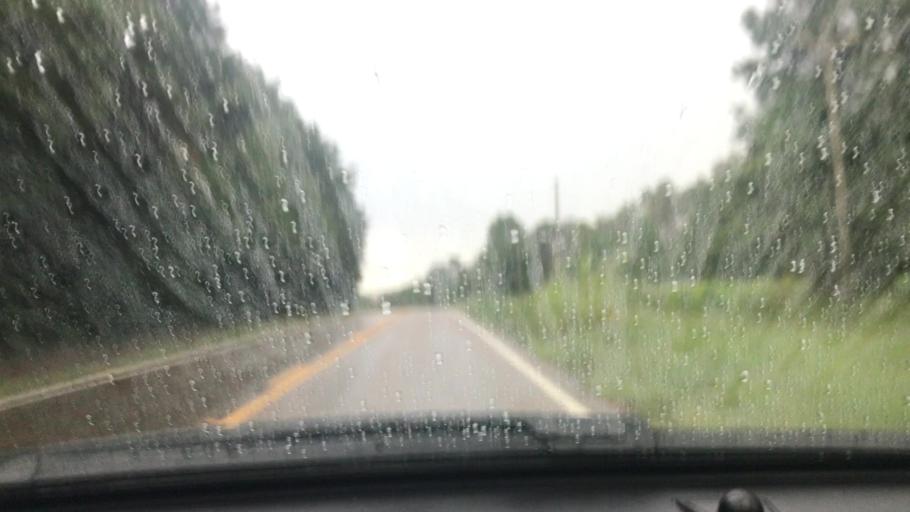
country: US
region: Mississippi
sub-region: Pike County
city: Summit
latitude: 31.3058
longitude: -90.5163
